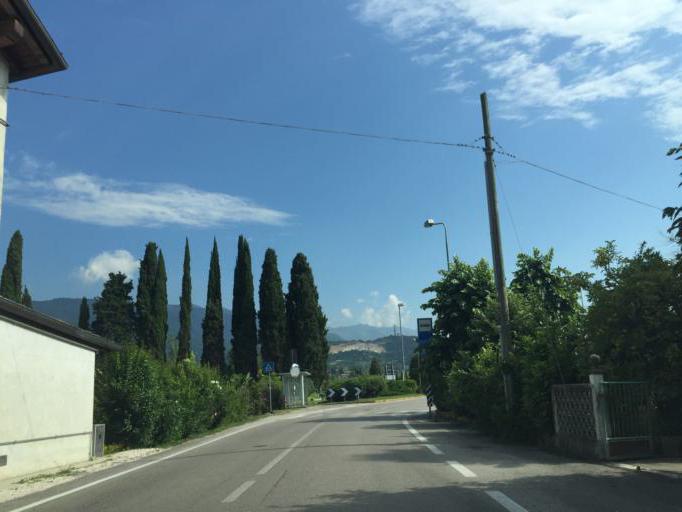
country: IT
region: Friuli Venezia Giulia
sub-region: Provincia di Pordenone
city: Caneva
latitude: 45.9615
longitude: 12.4485
